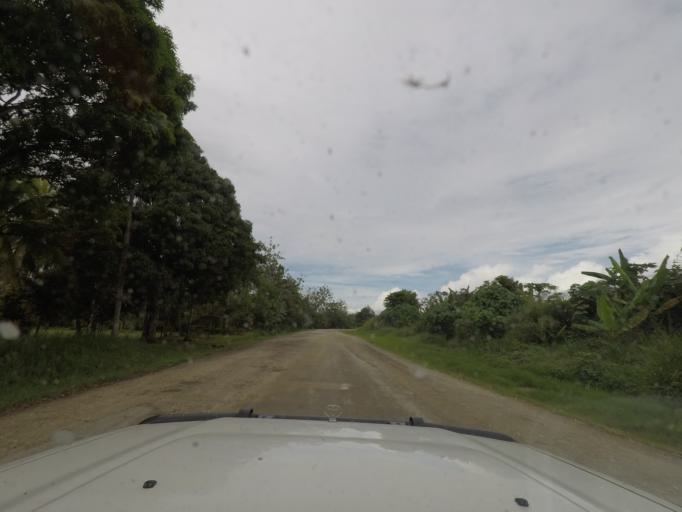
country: PG
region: Eastern Highlands
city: Goroka
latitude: -5.6539
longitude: 145.4961
